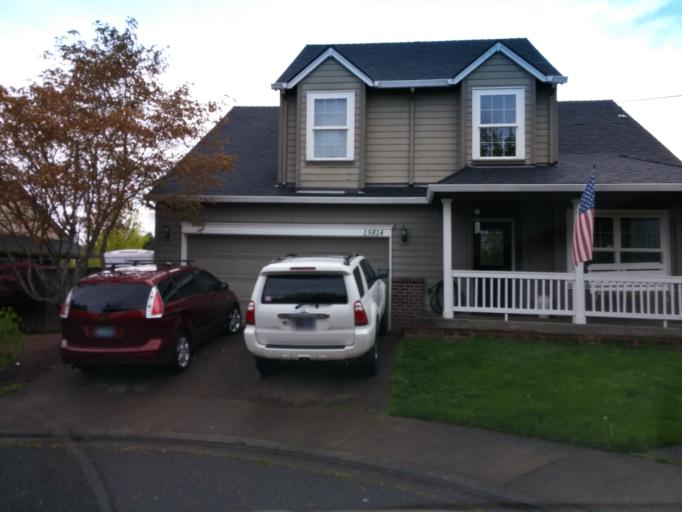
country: US
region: Oregon
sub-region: Washington County
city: Oak Hills
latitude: 45.5401
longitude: -122.8410
